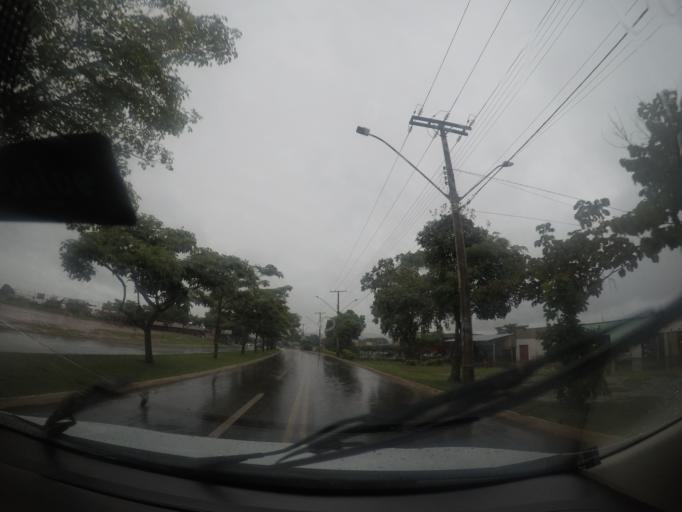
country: BR
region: Goias
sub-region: Goiania
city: Goiania
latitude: -16.6030
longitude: -49.3336
